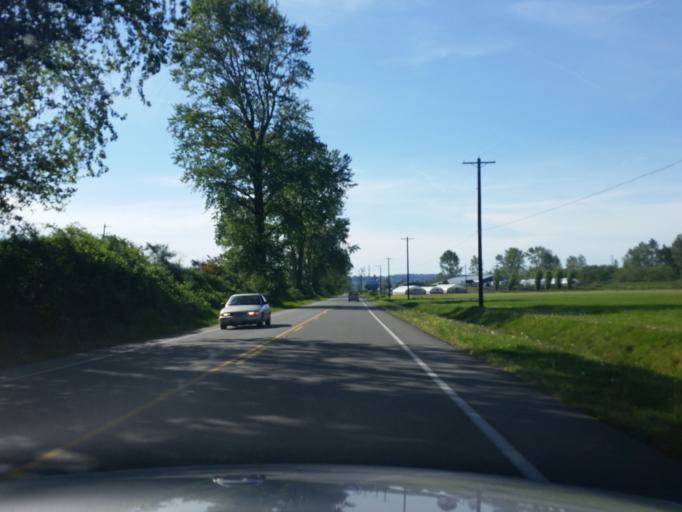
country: US
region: Washington
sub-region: Snohomish County
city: Snohomish
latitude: 47.9138
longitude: -122.1231
